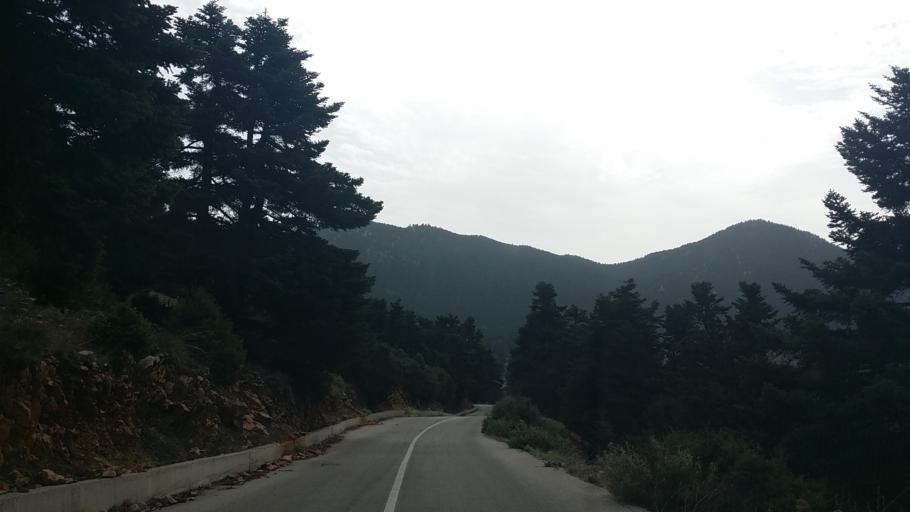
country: GR
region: Central Greece
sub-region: Nomos Voiotias
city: Livadeia
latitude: 38.3812
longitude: 22.8398
